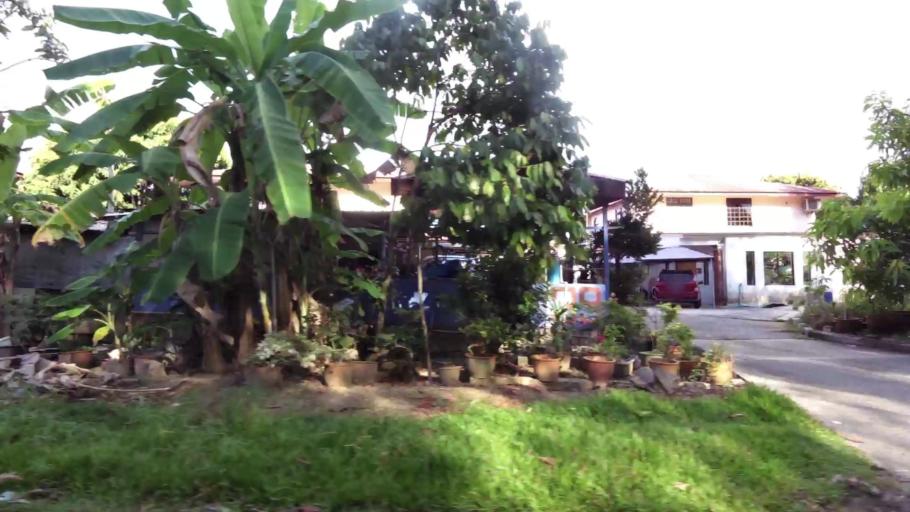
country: BN
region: Brunei and Muara
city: Bandar Seri Begawan
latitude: 4.9833
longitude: 114.9681
